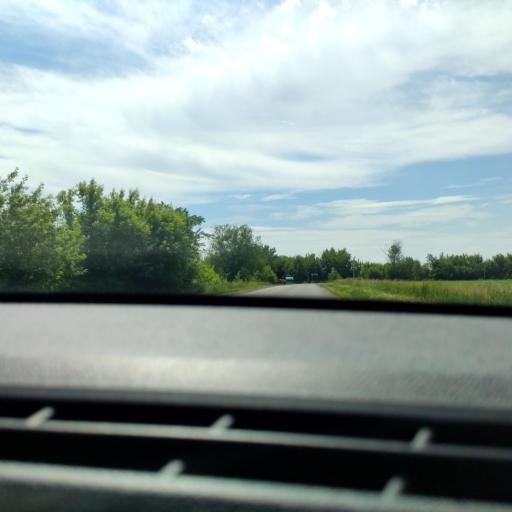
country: RU
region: Samara
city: Podstepki
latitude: 53.5231
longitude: 49.0976
